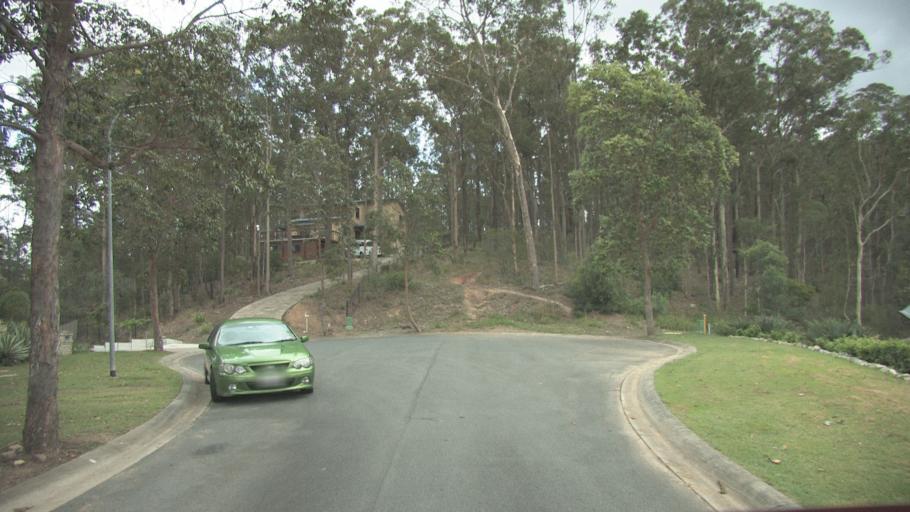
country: AU
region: Queensland
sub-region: Logan
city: Slacks Creek
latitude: -27.6380
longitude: 153.1739
